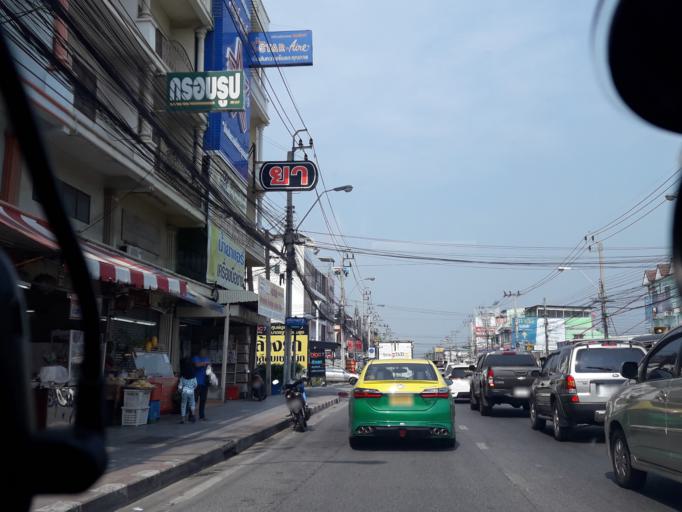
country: TH
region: Bangkok
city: Min Buri
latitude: 13.8221
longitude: 100.7206
